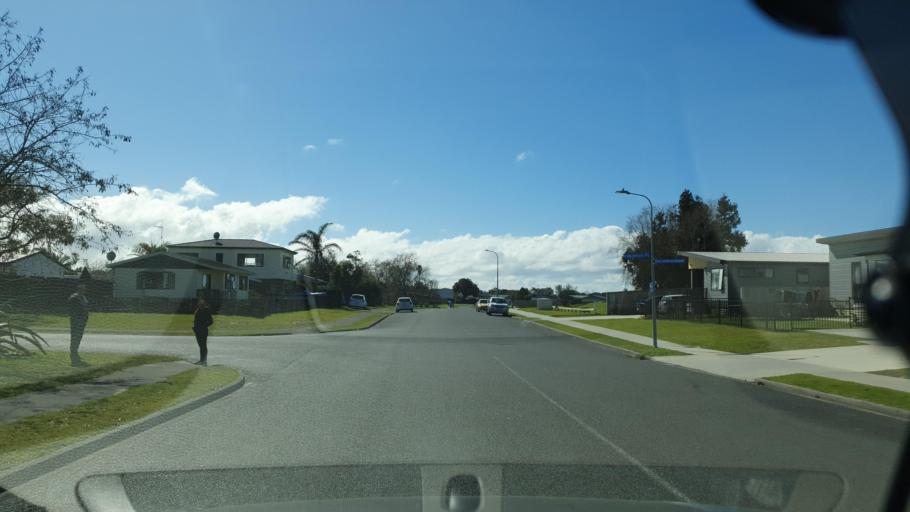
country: NZ
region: Bay of Plenty
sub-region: Tauranga City
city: Tauranga
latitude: -37.7064
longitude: 176.2906
